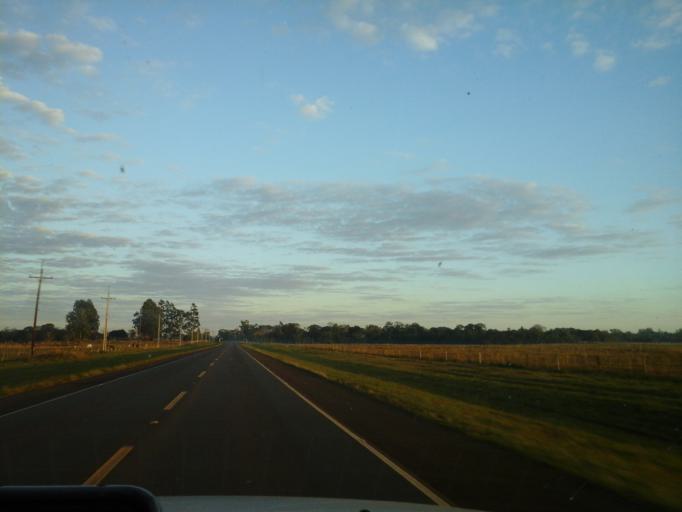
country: PY
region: Misiones
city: Santiago
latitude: -27.0395
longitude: -56.6649
